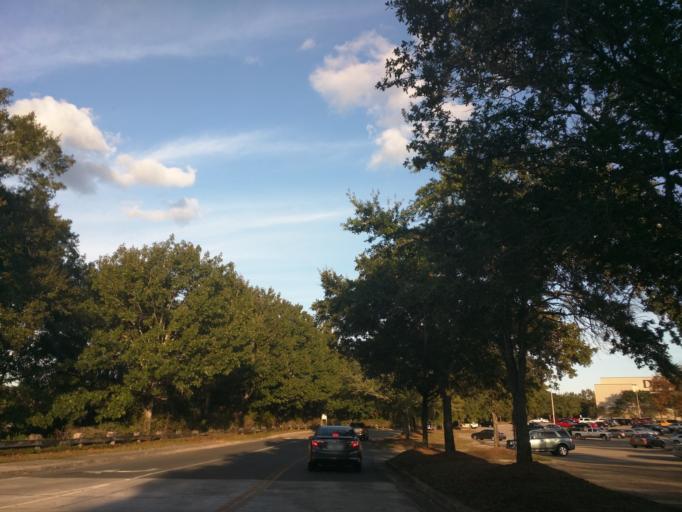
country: US
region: Florida
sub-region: Leon County
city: Tallahassee
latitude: 30.4386
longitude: -84.2558
